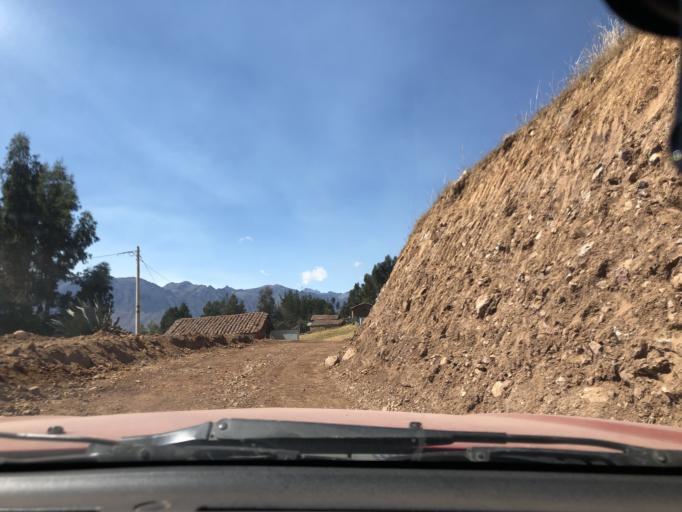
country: PE
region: Ayacucho
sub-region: Provincia de La Mar
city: Chilcas
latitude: -13.1695
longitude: -73.8530
